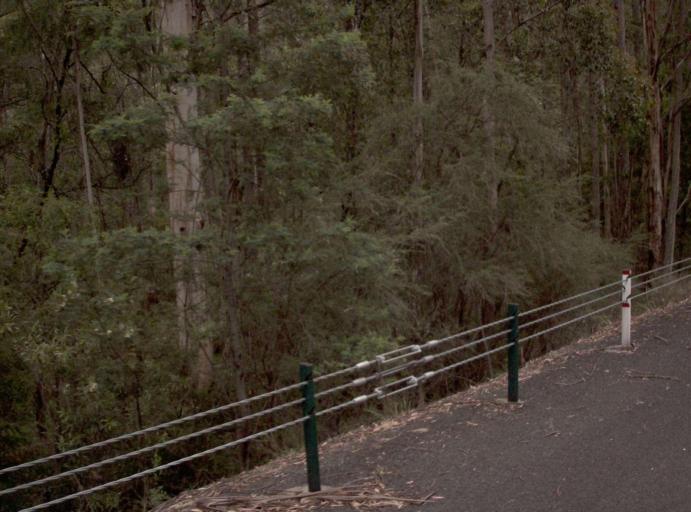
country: AU
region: New South Wales
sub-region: Bombala
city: Bombala
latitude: -37.3463
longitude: 149.2028
